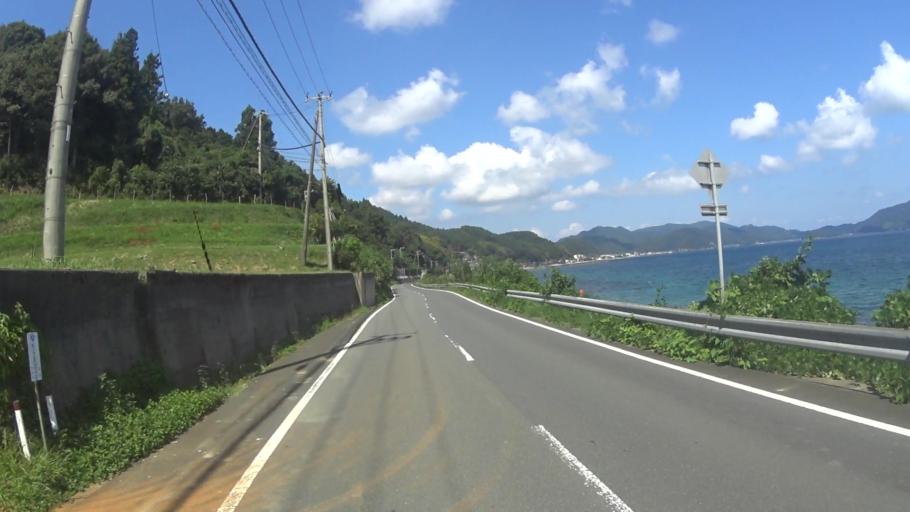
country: JP
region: Kyoto
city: Miyazu
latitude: 35.6416
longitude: 135.2504
